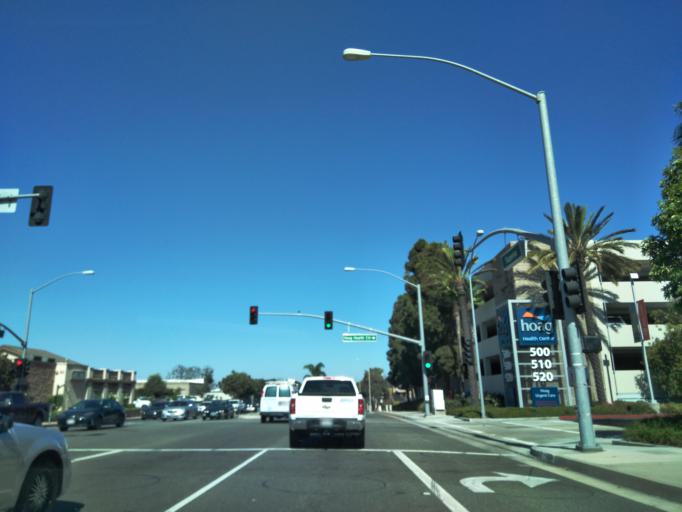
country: US
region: California
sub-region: Orange County
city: Newport Beach
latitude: 33.6304
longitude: -117.9292
